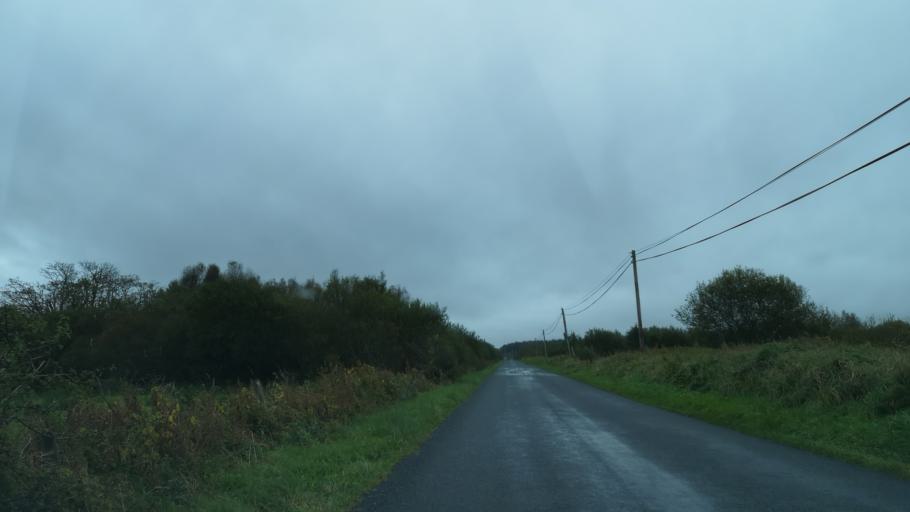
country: IE
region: Connaught
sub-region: Roscommon
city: Ballaghaderreen
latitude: 53.8929
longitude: -8.5738
